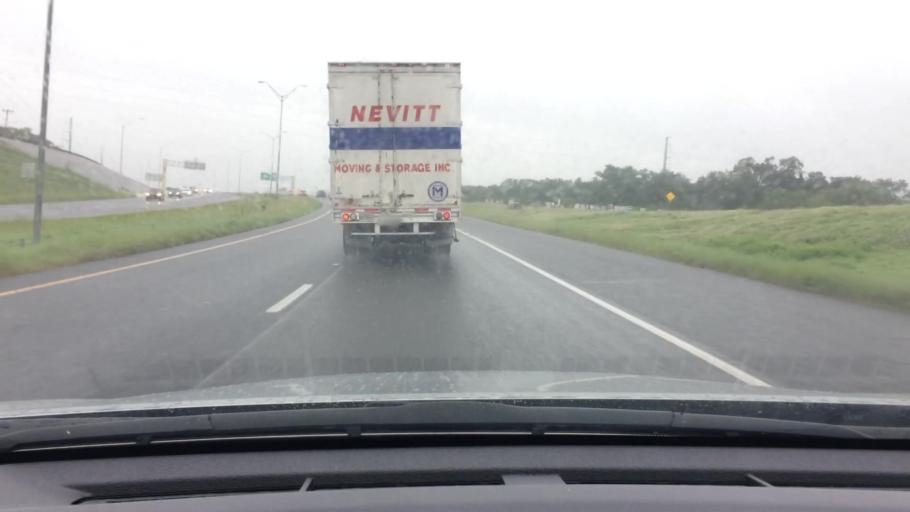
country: US
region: Texas
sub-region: Bexar County
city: Leon Valley
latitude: 29.4759
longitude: -98.6985
